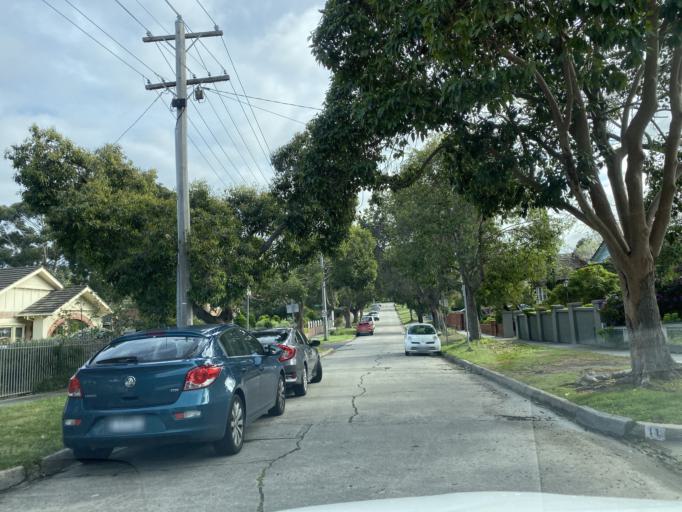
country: AU
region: Victoria
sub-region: Boroondara
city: Canterbury
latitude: -37.8332
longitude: 145.0839
